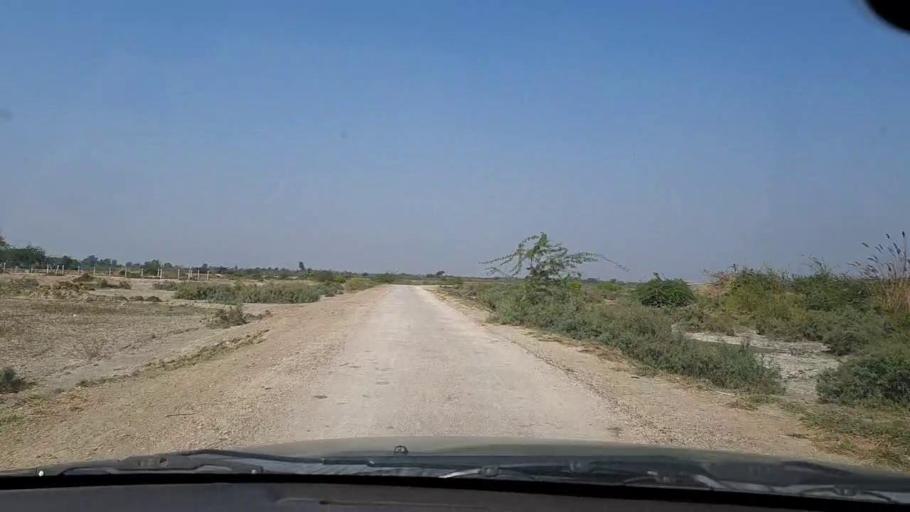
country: PK
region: Sindh
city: Chuhar Jamali
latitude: 24.4326
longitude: 67.7999
